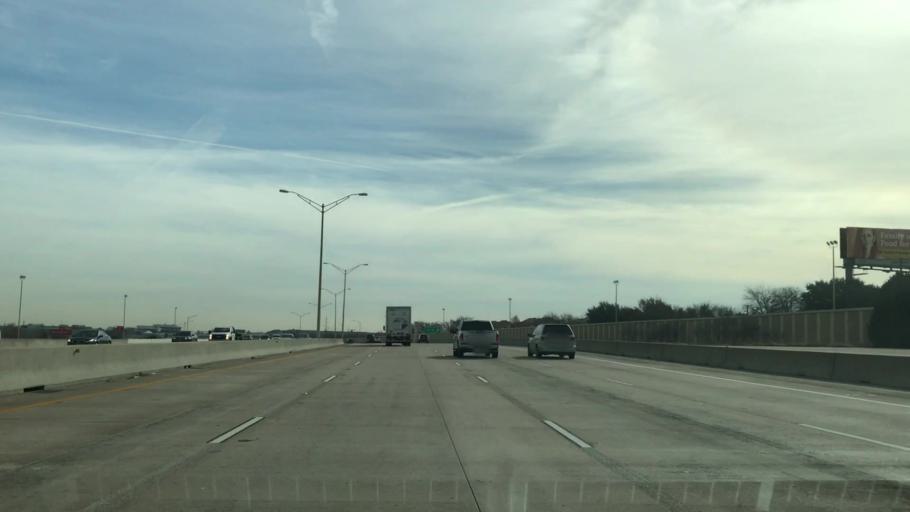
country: US
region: Texas
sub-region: Dallas County
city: Addison
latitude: 33.0021
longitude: -96.7760
